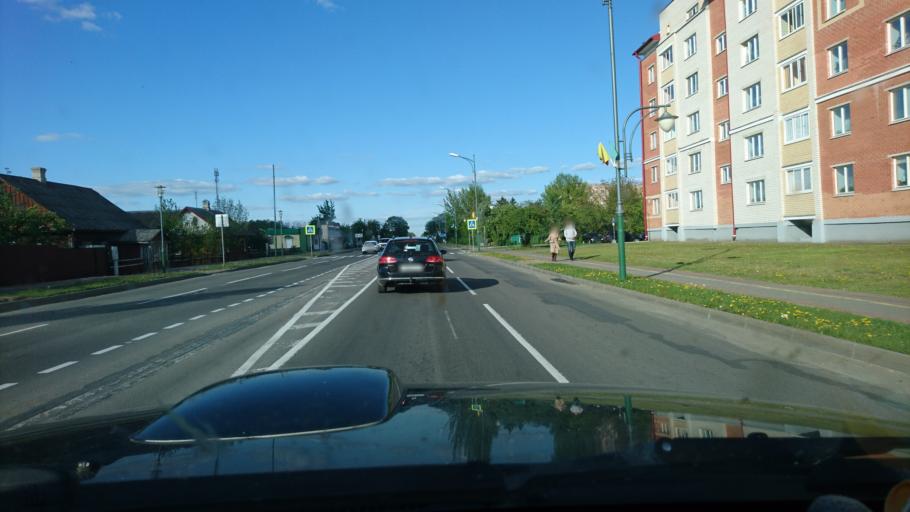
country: BY
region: Brest
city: Byaroza
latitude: 52.5378
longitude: 24.9917
